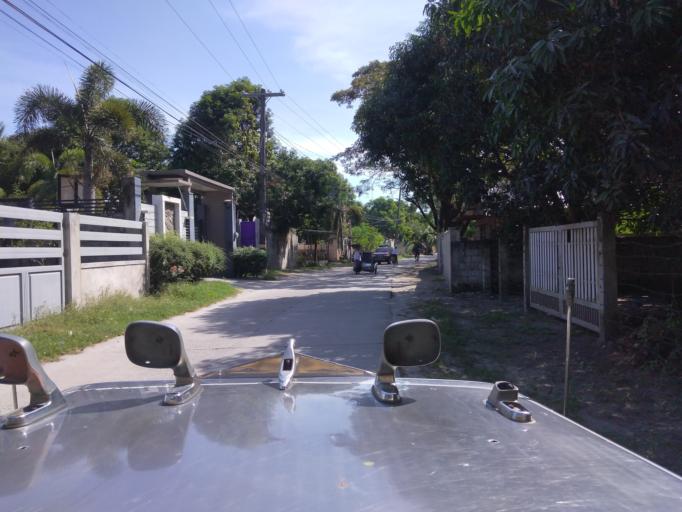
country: PH
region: Central Luzon
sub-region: Province of Pampanga
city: Bacolor
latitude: 15.0061
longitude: 120.6656
